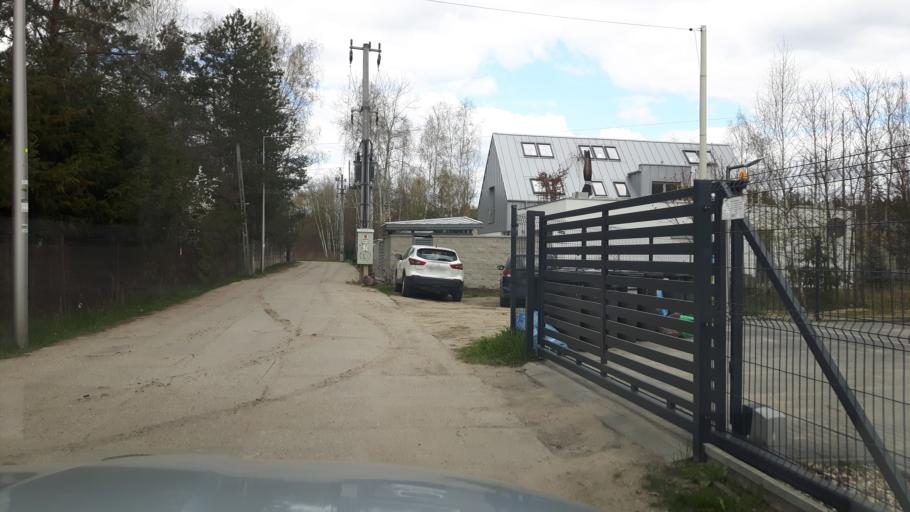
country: PL
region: Masovian Voivodeship
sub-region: Powiat wolominski
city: Kobylka
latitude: 52.3518
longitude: 21.2117
